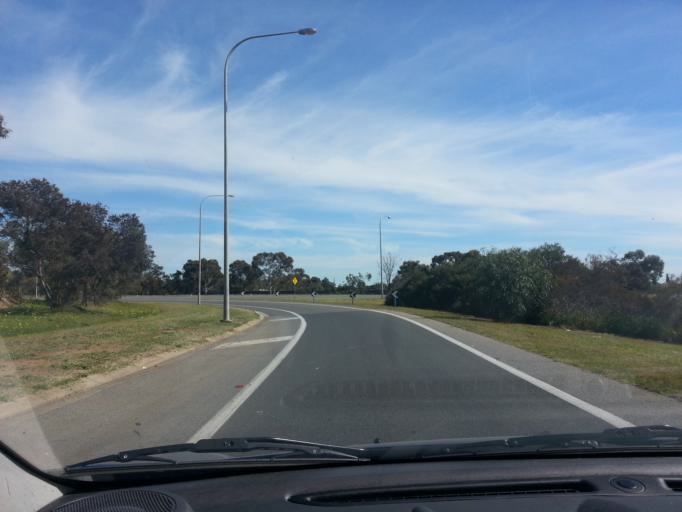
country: AU
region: South Australia
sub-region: Light
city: Willaston
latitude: -34.5823
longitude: 138.7356
